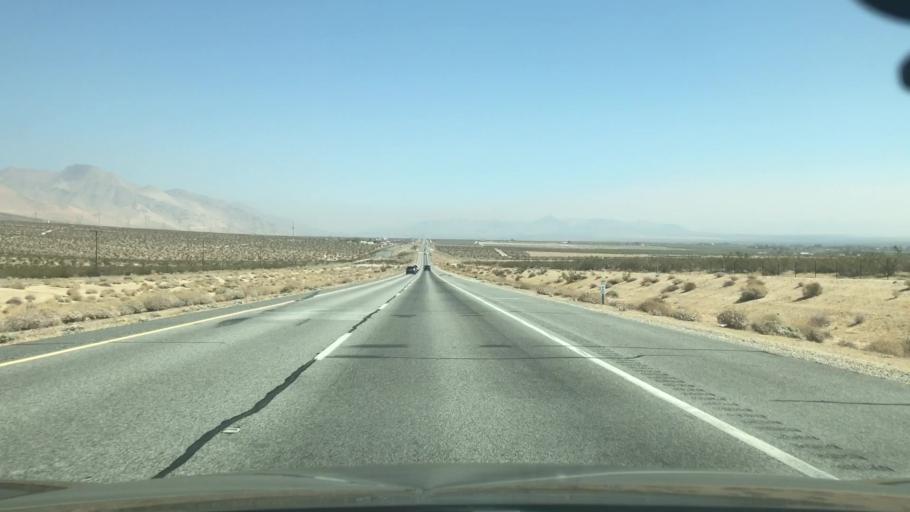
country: US
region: California
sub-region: Kern County
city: Inyokern
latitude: 35.6862
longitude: -117.8669
